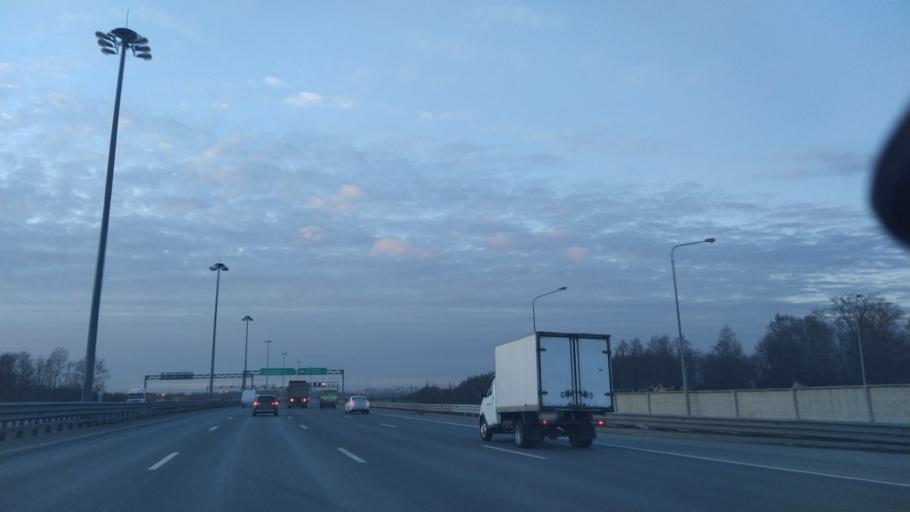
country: RU
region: St.-Petersburg
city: Krasnogvargeisky
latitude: 59.9913
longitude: 30.4821
